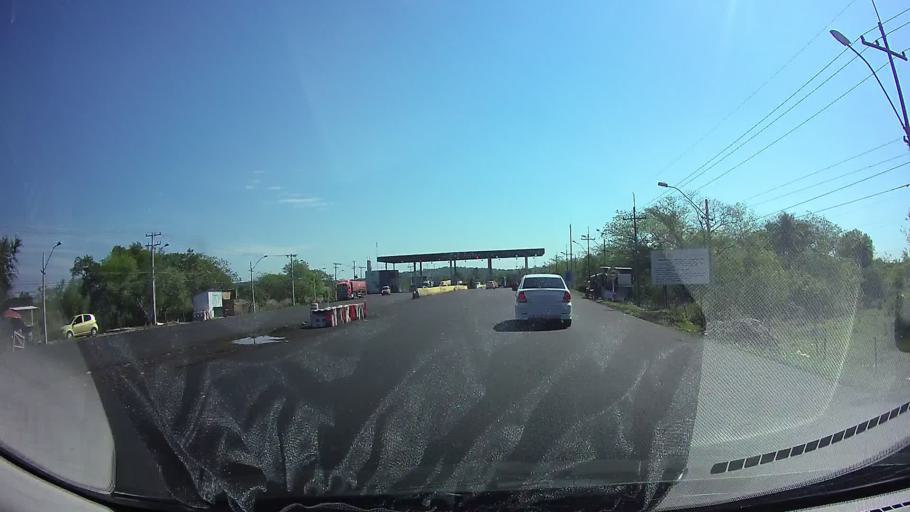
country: PY
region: Central
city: Ypacarai
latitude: -25.3888
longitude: -57.2701
